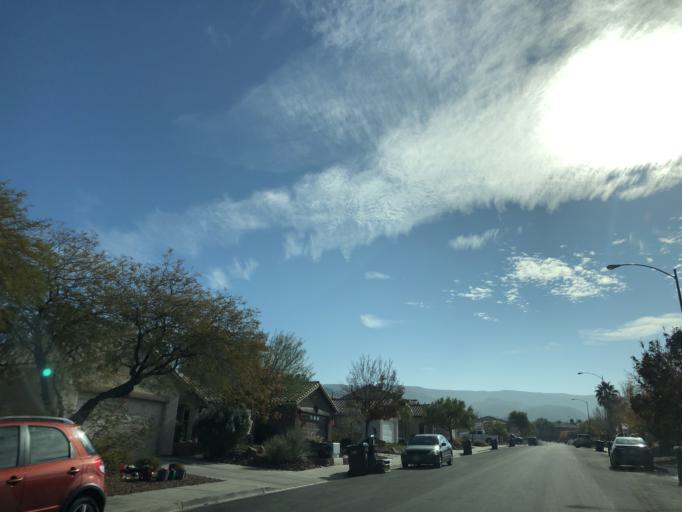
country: US
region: Nevada
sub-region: Clark County
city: Henderson
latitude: 36.0198
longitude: -115.0437
